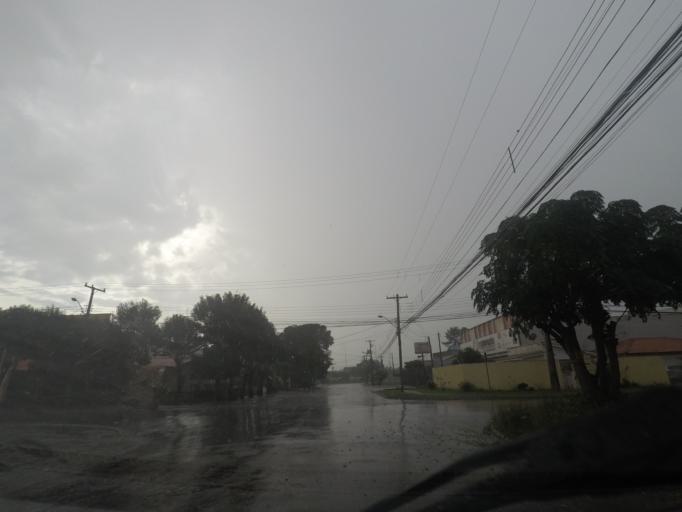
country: BR
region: Parana
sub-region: Curitiba
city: Curitiba
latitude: -25.4776
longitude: -49.2589
